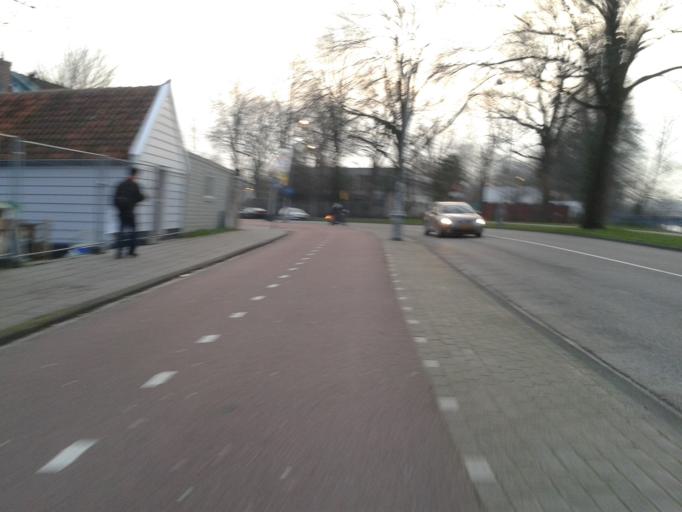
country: NL
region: North Holland
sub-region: Gemeente Amsterdam
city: Amsterdam
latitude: 52.3850
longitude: 4.9069
